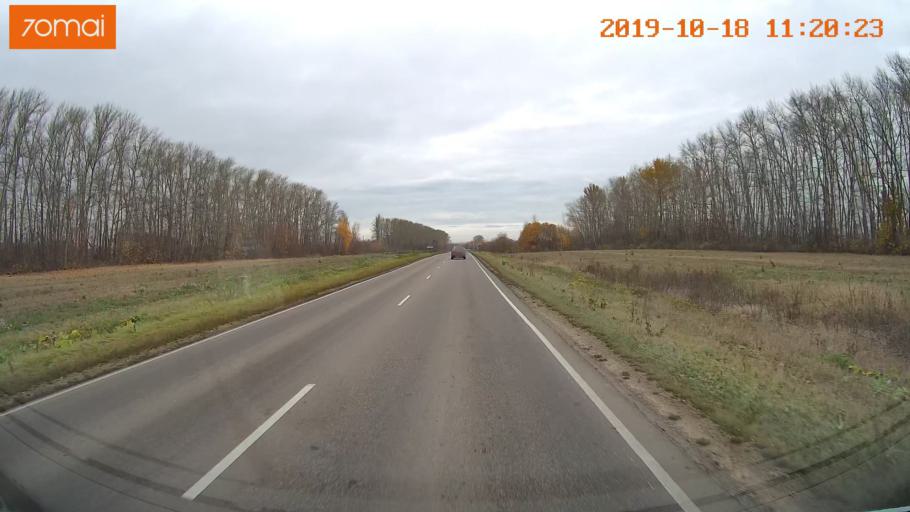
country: RU
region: Tula
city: Kimovsk
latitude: 54.0600
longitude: 38.5583
